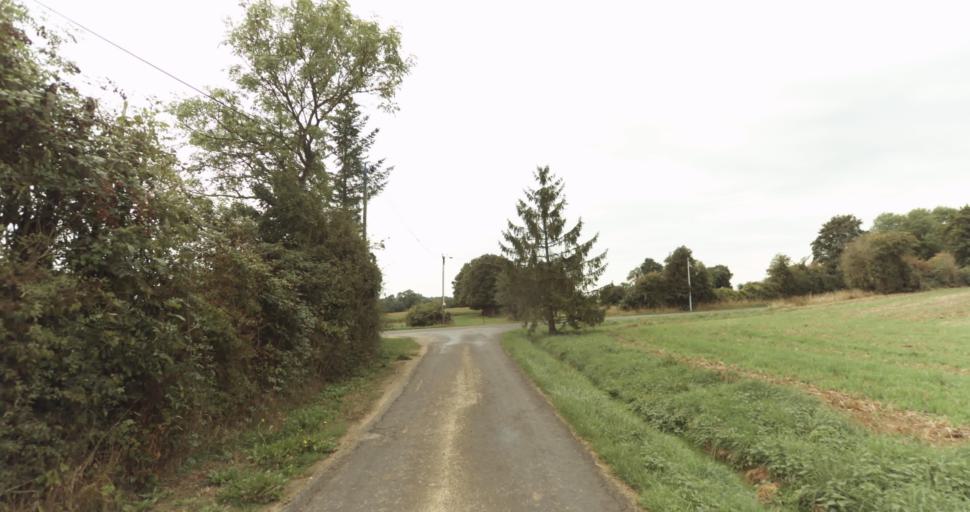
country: FR
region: Lower Normandy
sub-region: Departement de l'Orne
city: Gace
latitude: 48.7159
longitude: 0.3334
